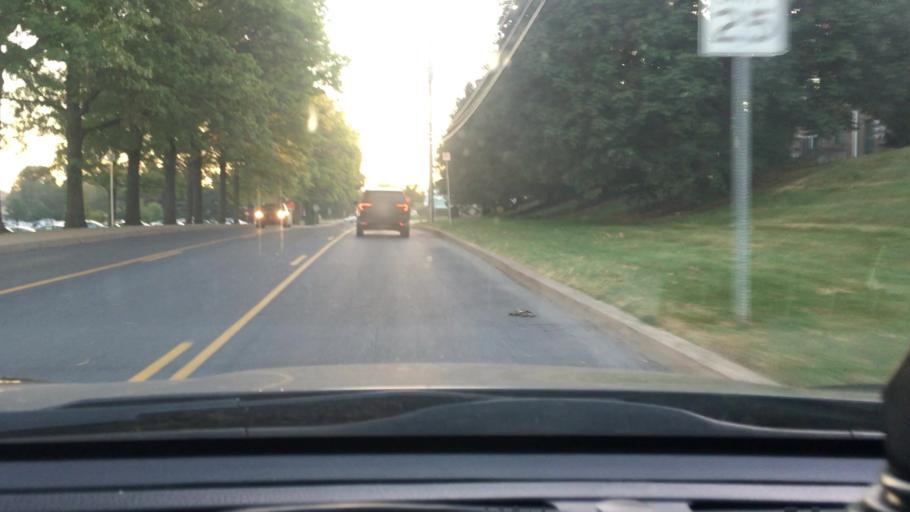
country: US
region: Pennsylvania
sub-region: Dauphin County
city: Progress
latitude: 40.2824
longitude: -76.8170
